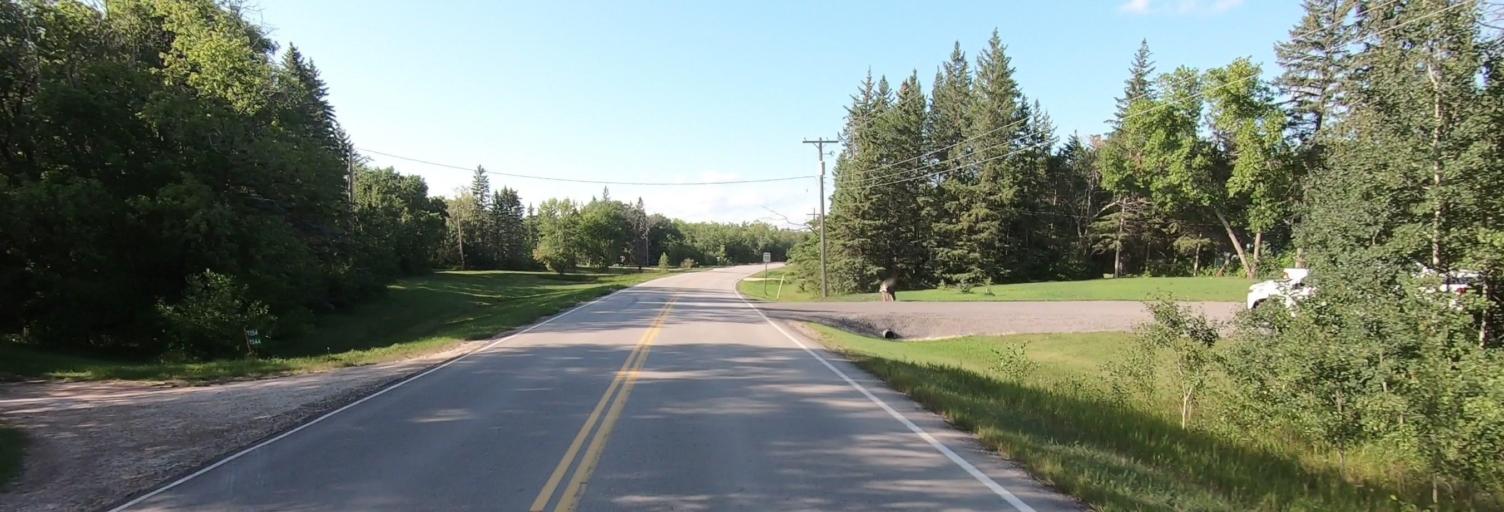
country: CA
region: Manitoba
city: Selkirk
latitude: 50.0950
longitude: -96.9325
